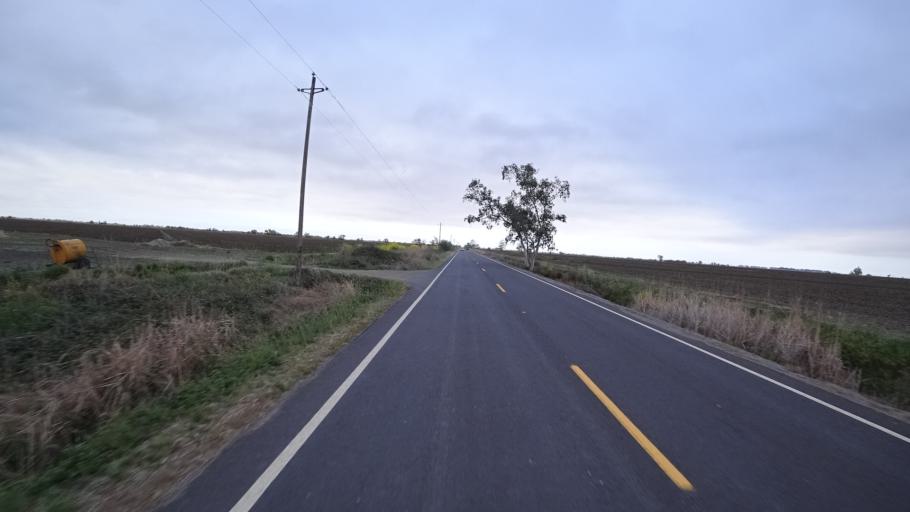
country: US
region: California
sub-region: Glenn County
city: Willows
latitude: 39.4064
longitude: -122.0729
